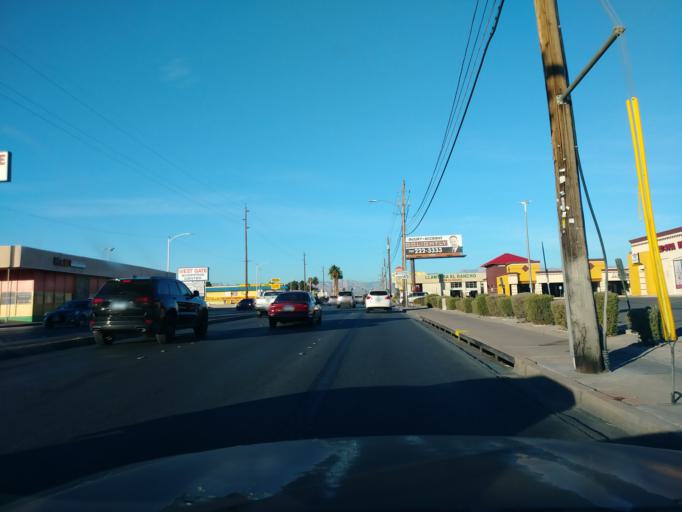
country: US
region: Nevada
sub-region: Clark County
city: Las Vegas
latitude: 36.1591
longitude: -115.1927
